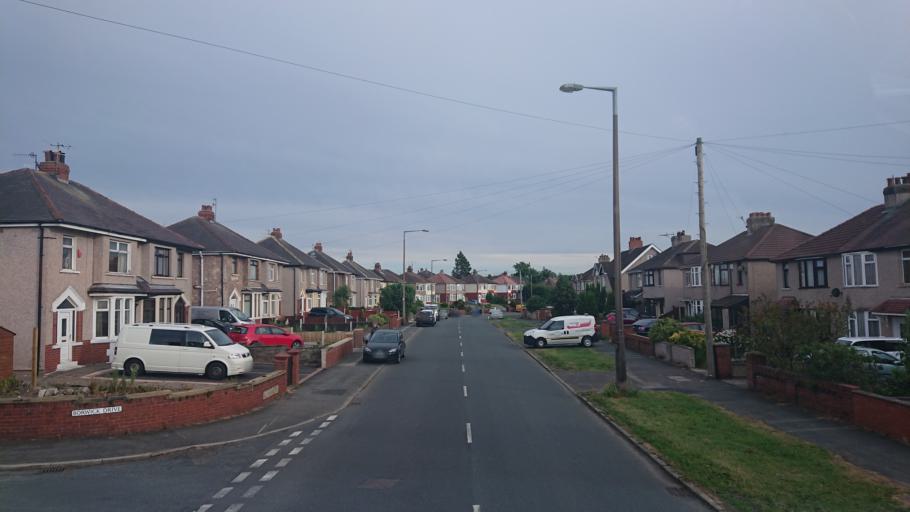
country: GB
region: England
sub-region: Lancashire
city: Lancaster
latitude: 54.0587
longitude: -2.8169
